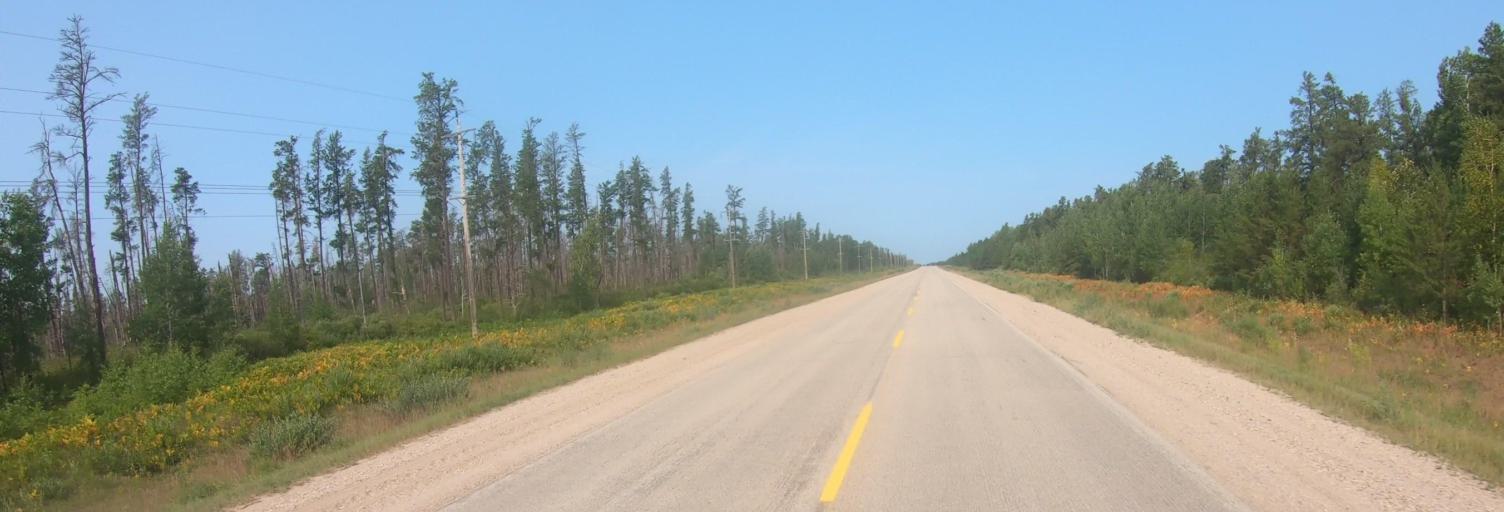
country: US
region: Minnesota
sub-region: Roseau County
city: Roseau
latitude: 49.0791
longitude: -95.8668
